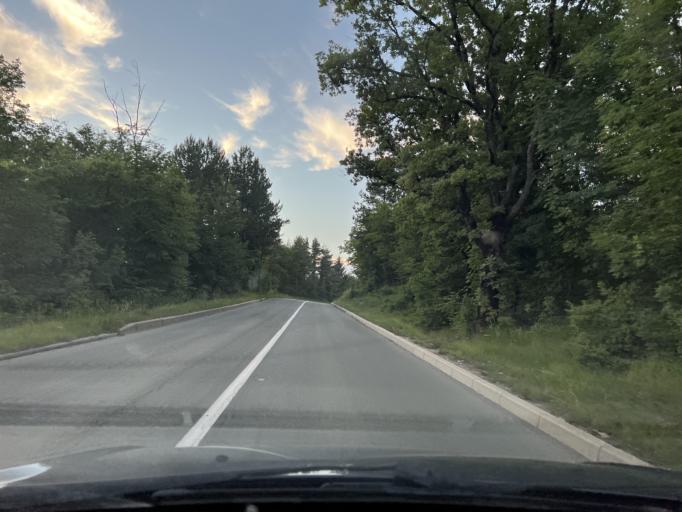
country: HR
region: Primorsko-Goranska
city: Klana
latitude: 45.4237
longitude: 14.3770
